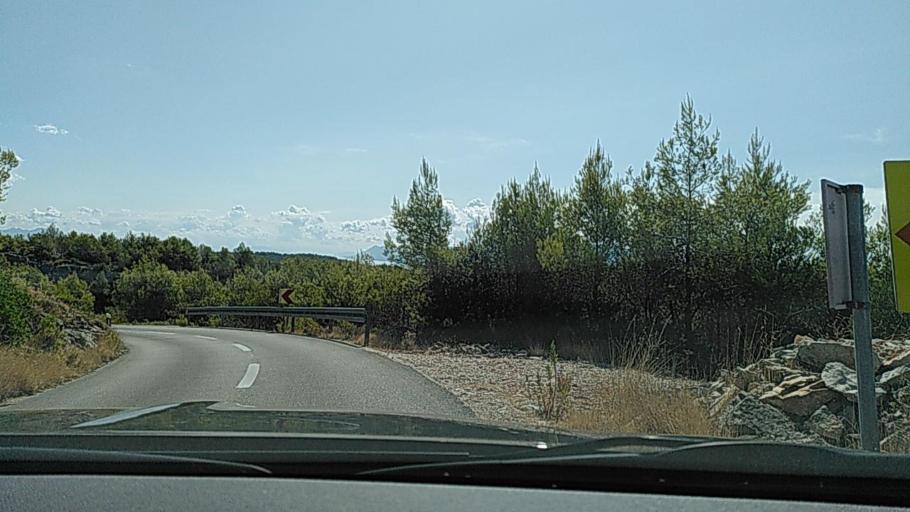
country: HR
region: Splitsko-Dalmatinska
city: Tucepi
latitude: 43.1327
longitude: 16.9787
